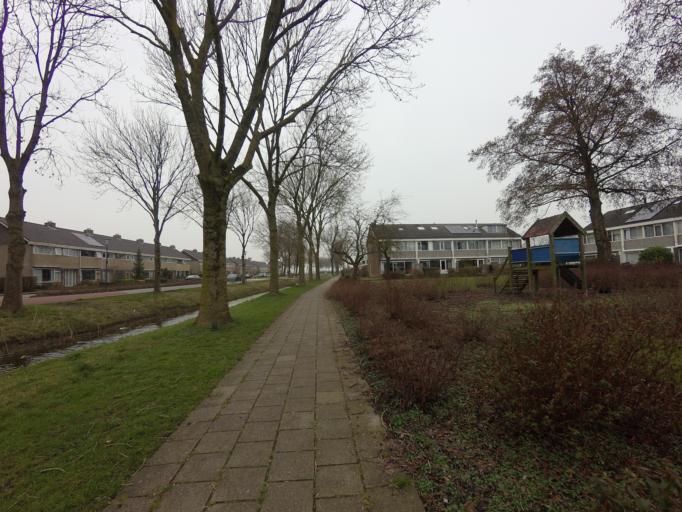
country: NL
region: Friesland
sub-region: Gemeente Franekeradeel
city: Franeker
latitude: 53.1908
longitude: 5.5616
